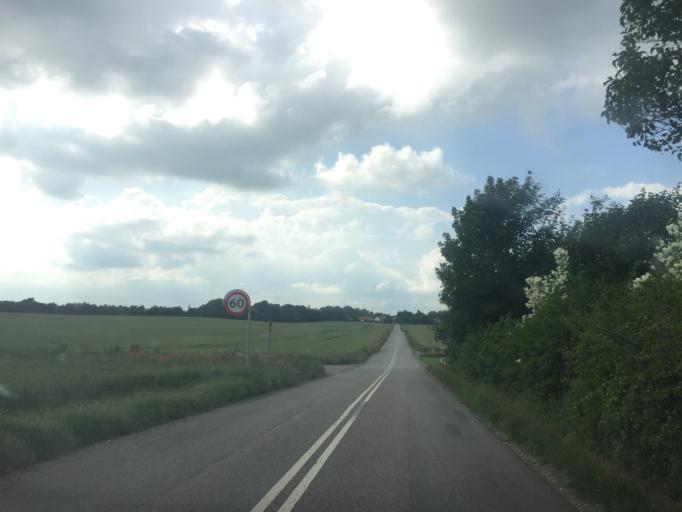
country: DK
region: Capital Region
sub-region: Hoje-Taastrup Kommune
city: Flong
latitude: 55.6887
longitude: 12.1748
